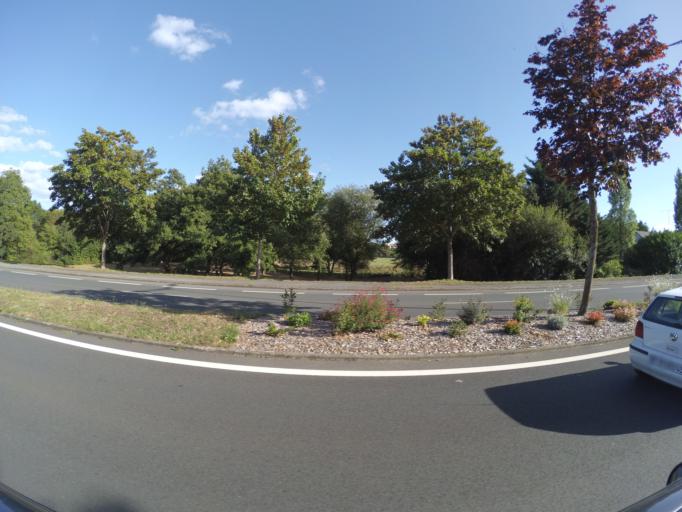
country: FR
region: Pays de la Loire
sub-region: Departement de Maine-et-Loire
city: Cholet
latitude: 47.0489
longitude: -0.8738
